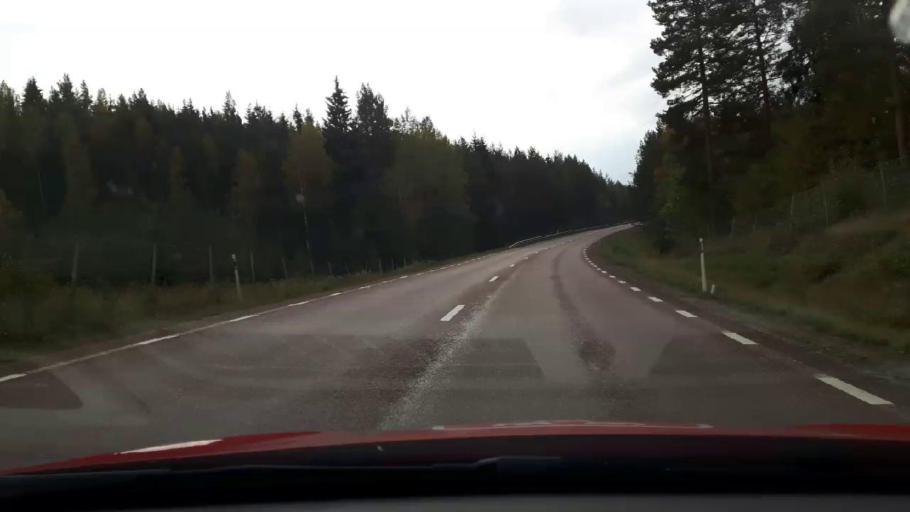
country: SE
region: Gaevleborg
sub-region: Bollnas Kommun
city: Kilafors
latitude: 61.2605
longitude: 16.5528
